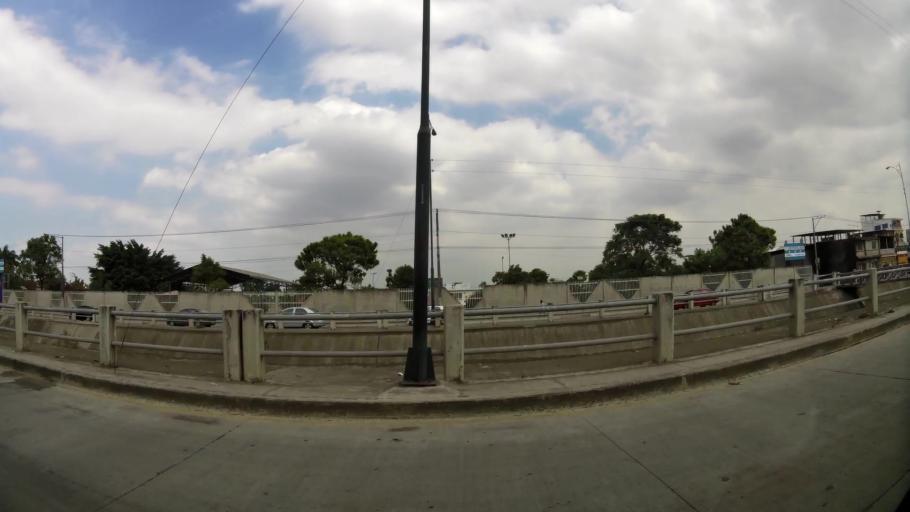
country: EC
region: Guayas
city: Eloy Alfaro
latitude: -2.0888
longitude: -79.9302
